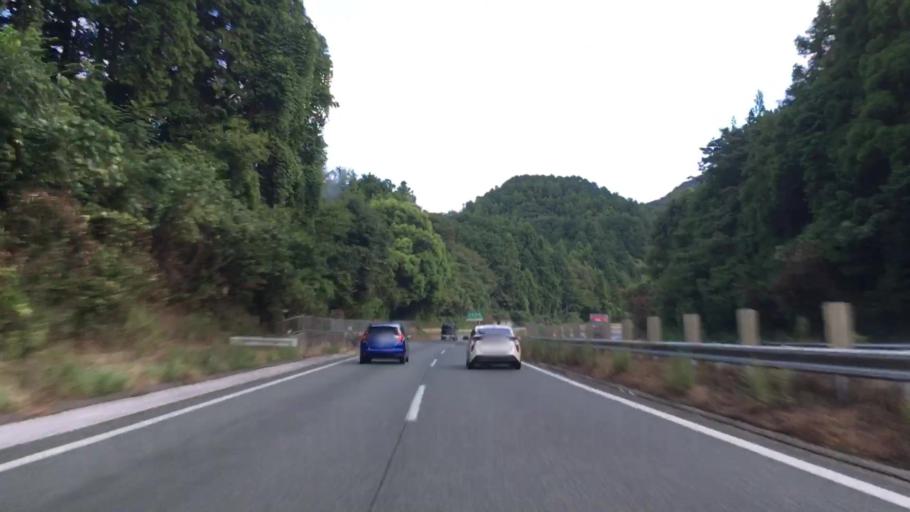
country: JP
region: Yamaguchi
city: Ogori-shimogo
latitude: 34.1652
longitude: 131.2411
